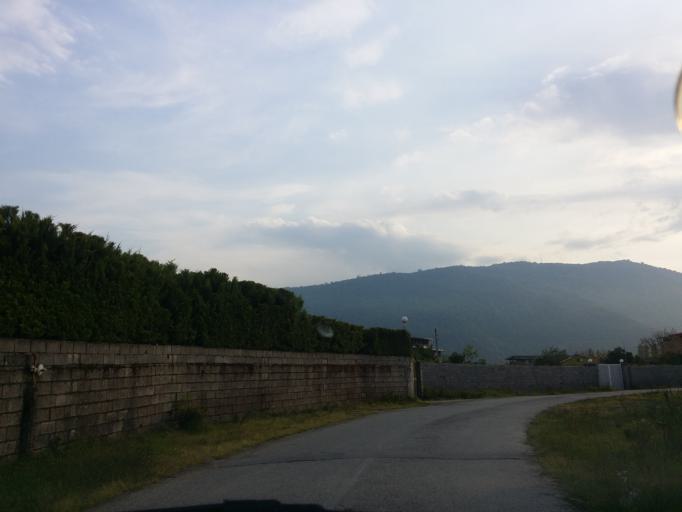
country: IR
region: Mazandaran
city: Chalus
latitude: 36.6688
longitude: 51.3674
